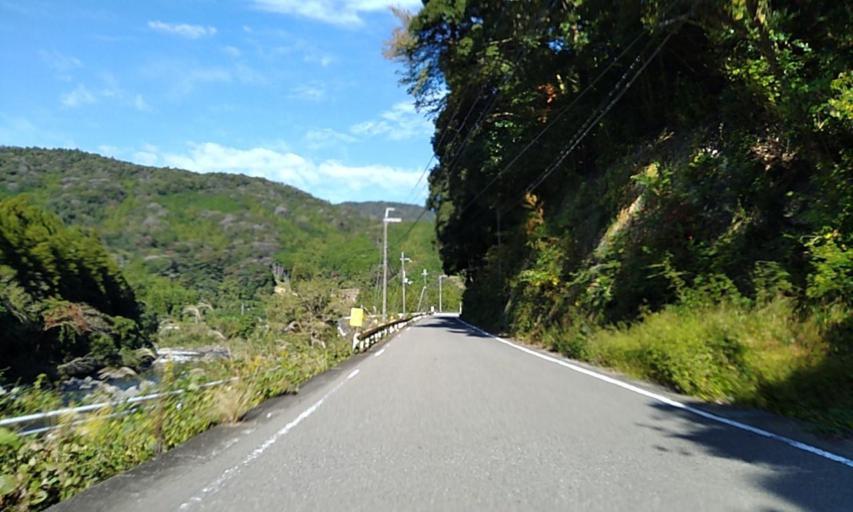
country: JP
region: Wakayama
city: Kainan
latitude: 34.0499
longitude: 135.3101
